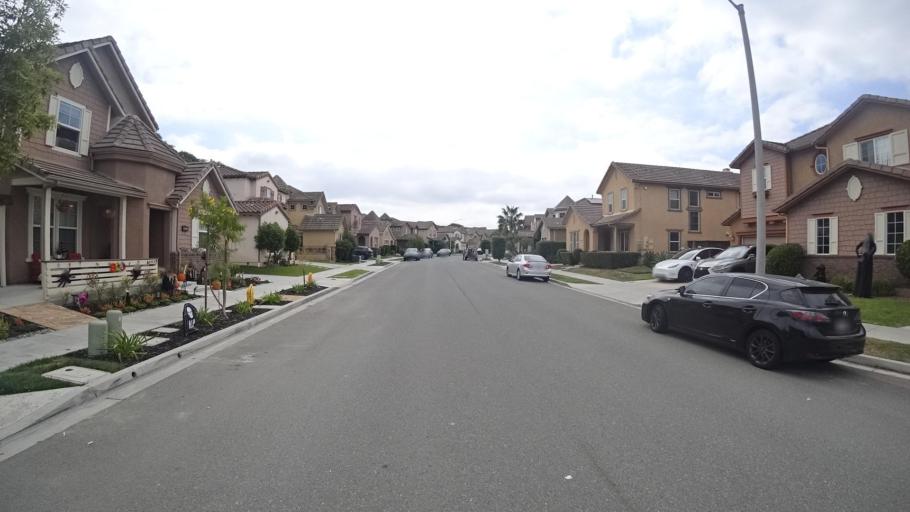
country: US
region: California
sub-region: San Diego County
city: Fairbanks Ranch
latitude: 33.0239
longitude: -117.1157
